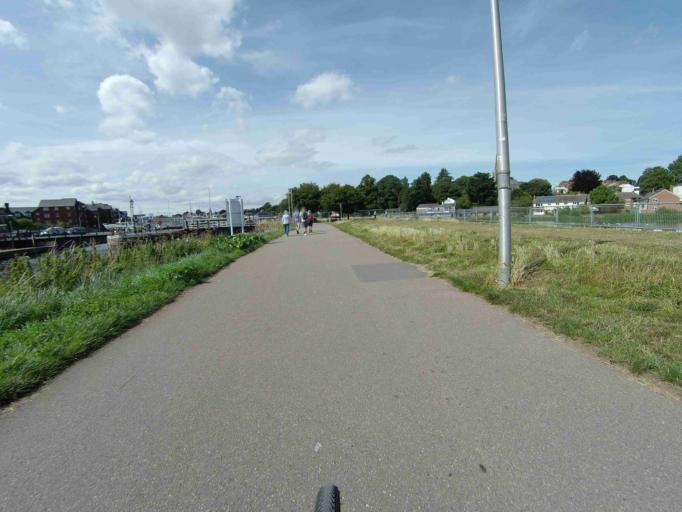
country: GB
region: England
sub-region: Devon
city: Exeter
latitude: 50.7144
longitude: -3.5268
